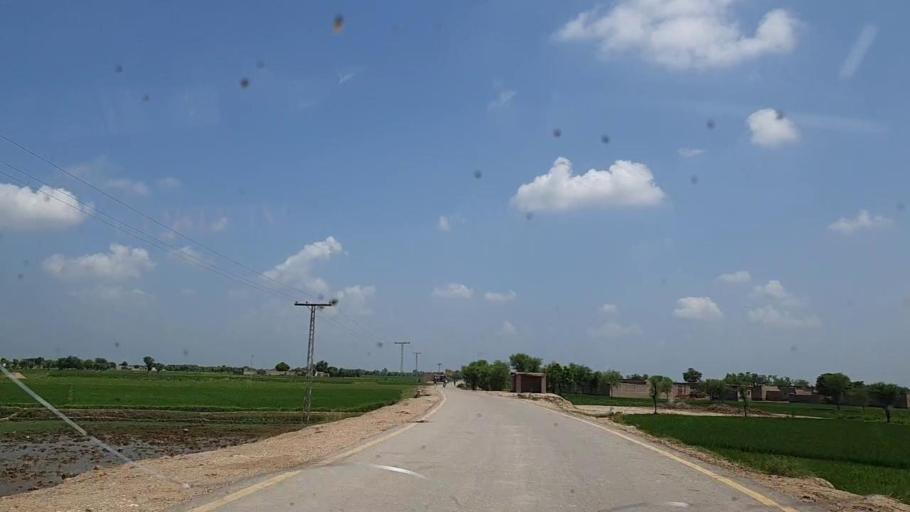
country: PK
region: Sindh
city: Tharu Shah
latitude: 26.9848
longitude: 68.0791
